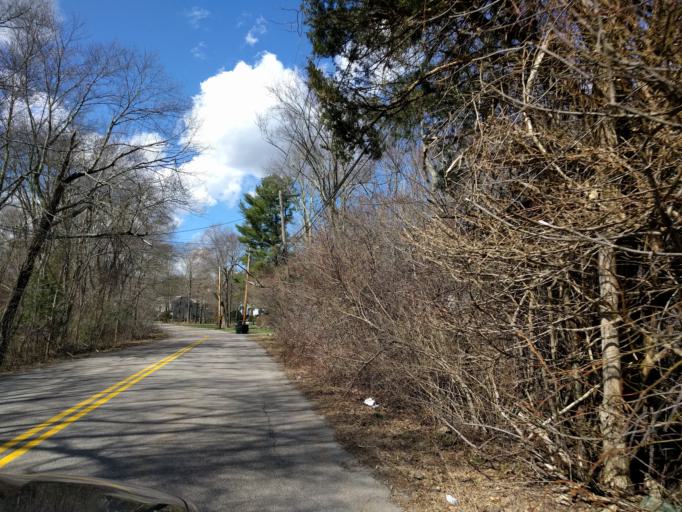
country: US
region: Massachusetts
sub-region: Norfolk County
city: Millis-Clicquot
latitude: 42.1449
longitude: -71.3504
